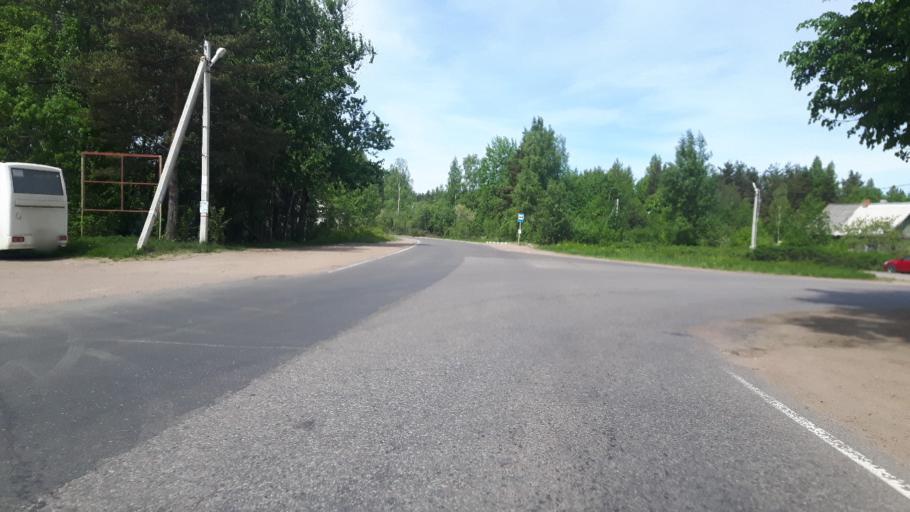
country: RU
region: Leningrad
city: Ust'-Luga
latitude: 59.6563
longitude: 28.2539
